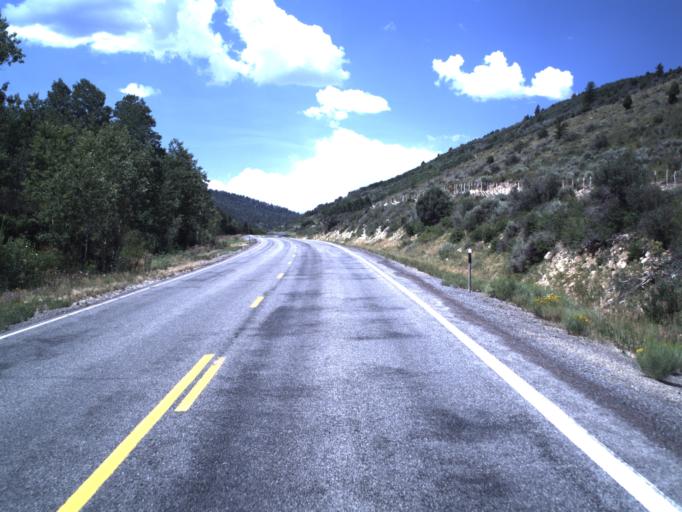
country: US
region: Utah
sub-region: Carbon County
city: Helper
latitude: 39.8576
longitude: -111.0598
